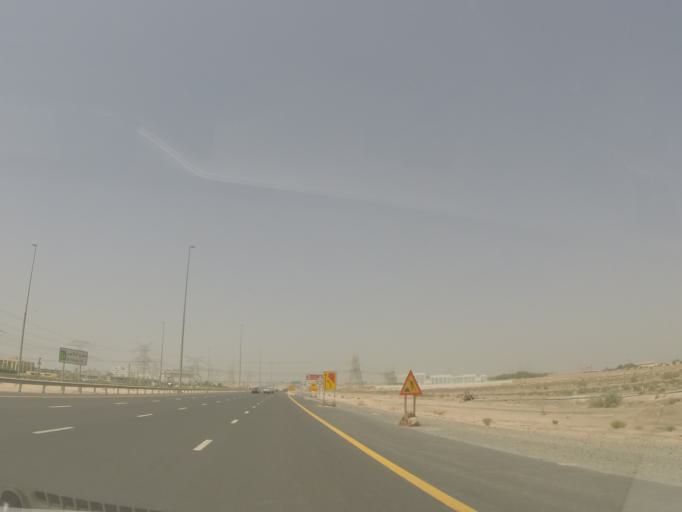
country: AE
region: Dubai
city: Dubai
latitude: 25.0057
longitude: 55.1725
